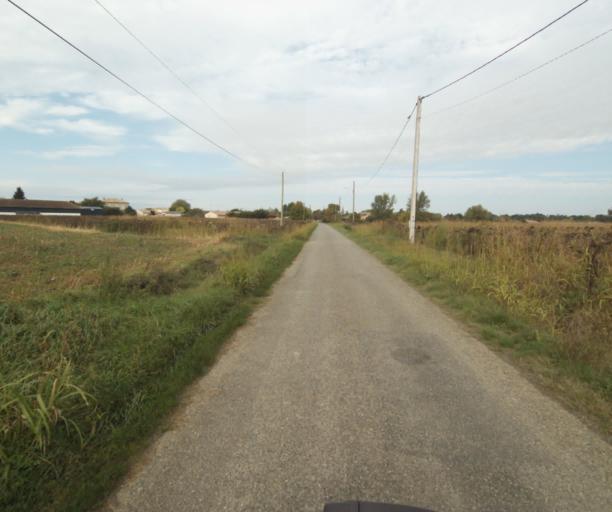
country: FR
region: Midi-Pyrenees
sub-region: Departement du Tarn-et-Garonne
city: Finhan
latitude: 43.9076
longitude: 1.2296
